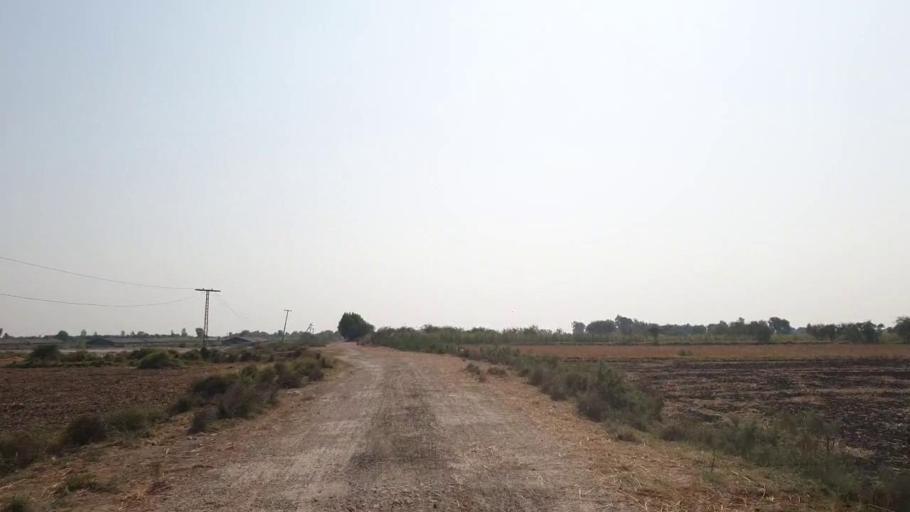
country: PK
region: Sindh
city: Tando Muhammad Khan
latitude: 25.0443
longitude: 68.4526
